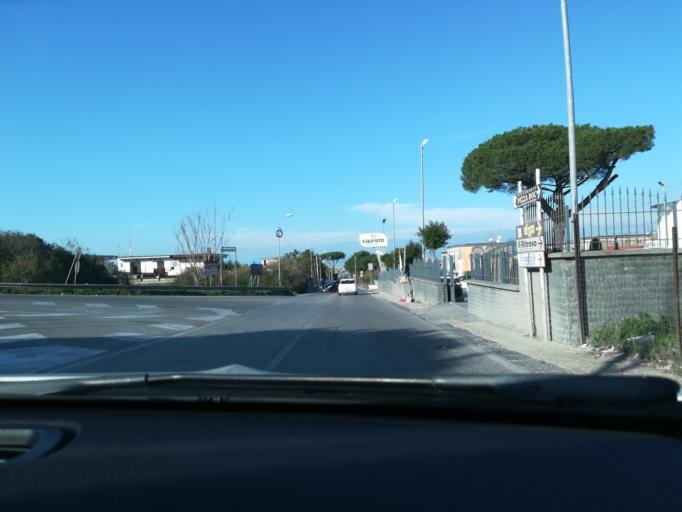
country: IT
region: Campania
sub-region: Provincia di Napoli
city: Sant'Anastasia
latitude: 40.8791
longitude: 14.3987
